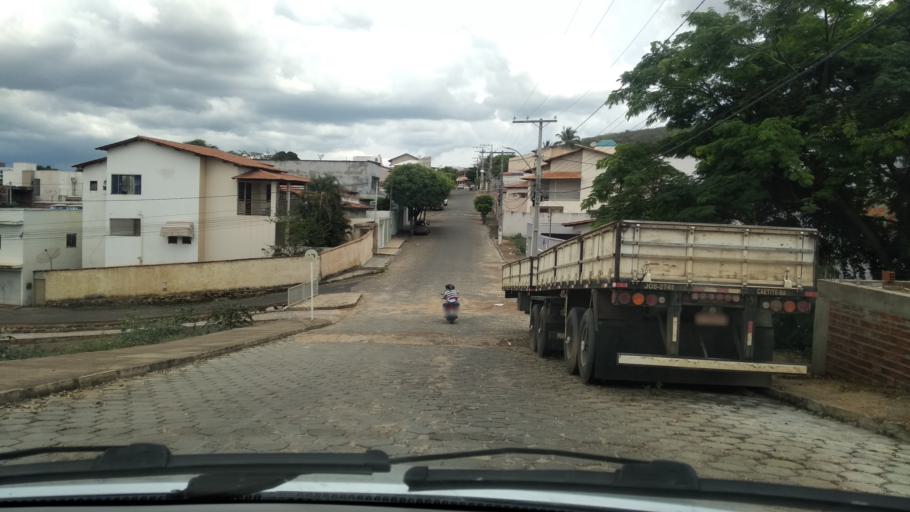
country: BR
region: Bahia
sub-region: Caetite
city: Caetite
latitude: -14.0707
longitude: -42.4831
